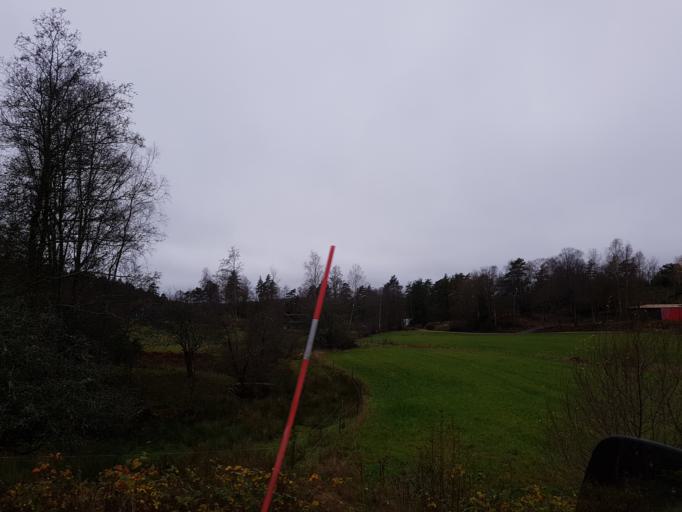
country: SE
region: Vaestra Goetaland
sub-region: Orust
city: Henan
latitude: 58.2272
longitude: 11.7655
